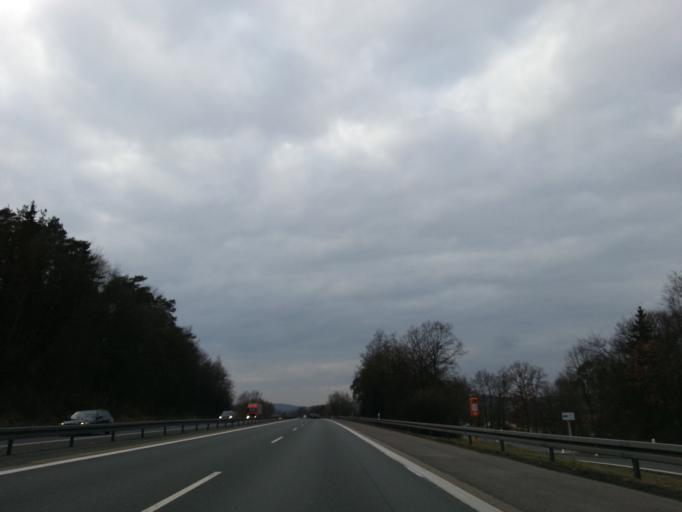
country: DE
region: Bavaria
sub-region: Regierungsbezirk Mittelfranken
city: Burghaslach
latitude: 49.7610
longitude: 10.5578
